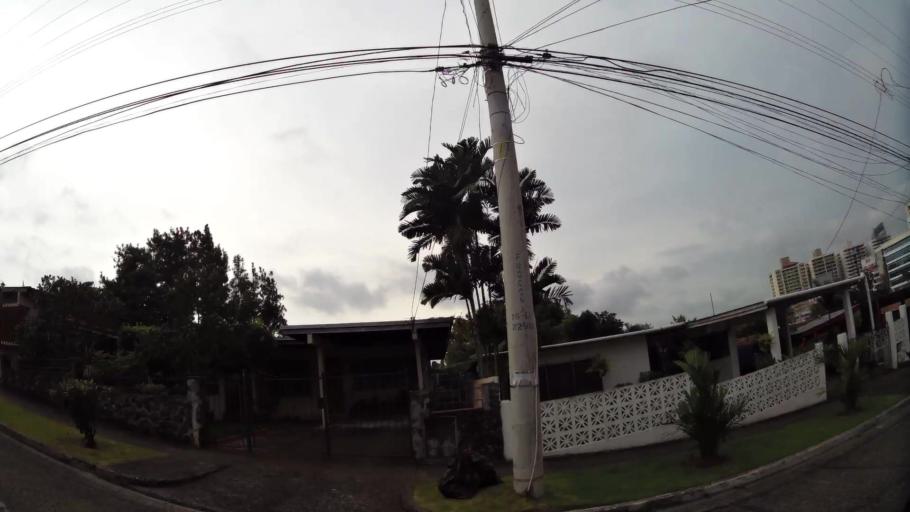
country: PA
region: Panama
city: Panama
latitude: 9.0103
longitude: -79.5327
